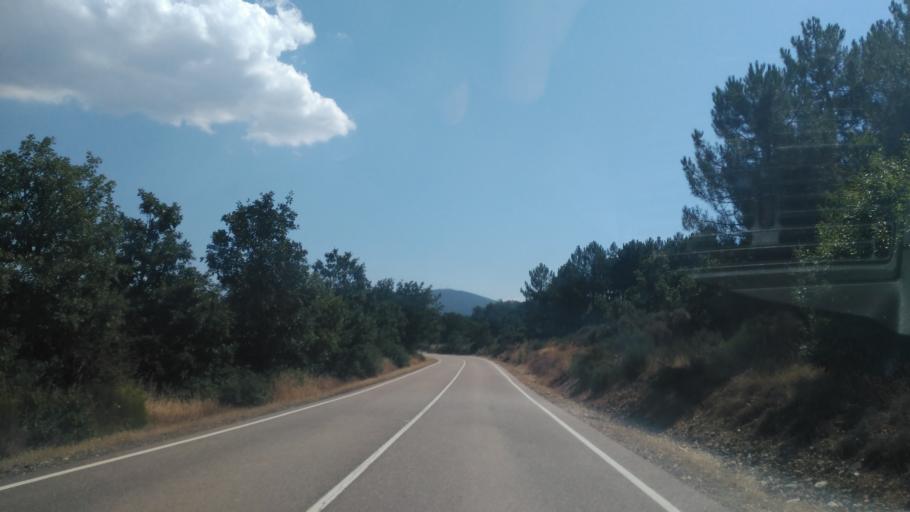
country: ES
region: Castille and Leon
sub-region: Provincia de Salamanca
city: Cereceda de la Sierra
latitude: 40.5670
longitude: -6.1021
